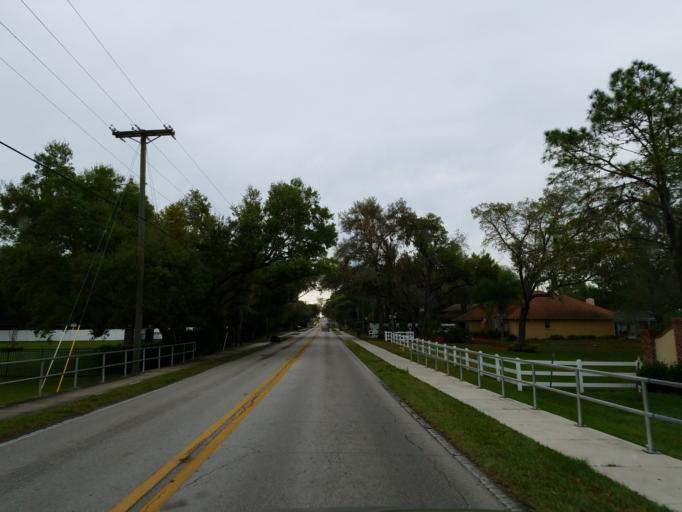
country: US
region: Florida
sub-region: Hillsborough County
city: Bloomingdale
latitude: 27.9016
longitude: -82.2442
